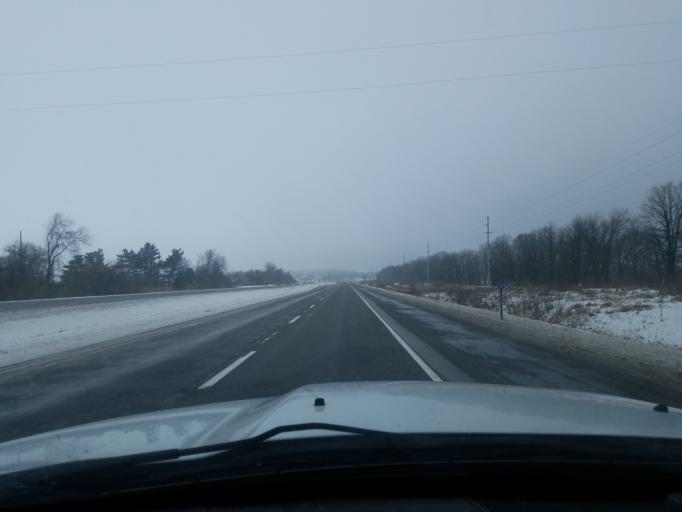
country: US
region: Indiana
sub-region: Fulton County
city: Rochester
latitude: 41.0257
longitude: -86.1794
